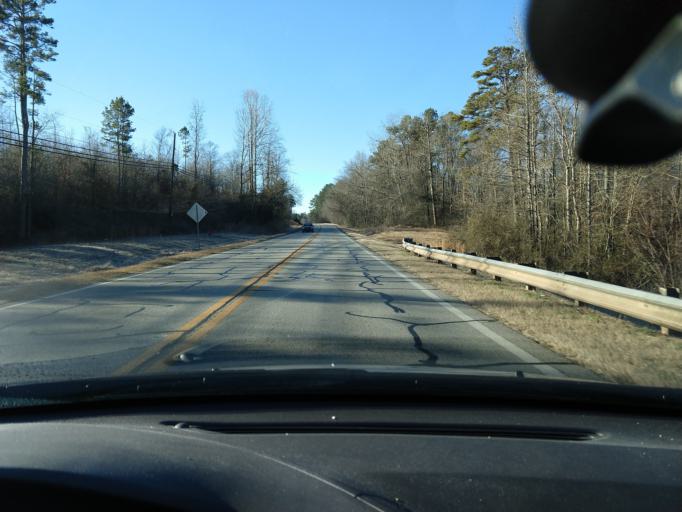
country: US
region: Georgia
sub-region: Jackson County
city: Commerce
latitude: 34.2234
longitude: -83.4569
